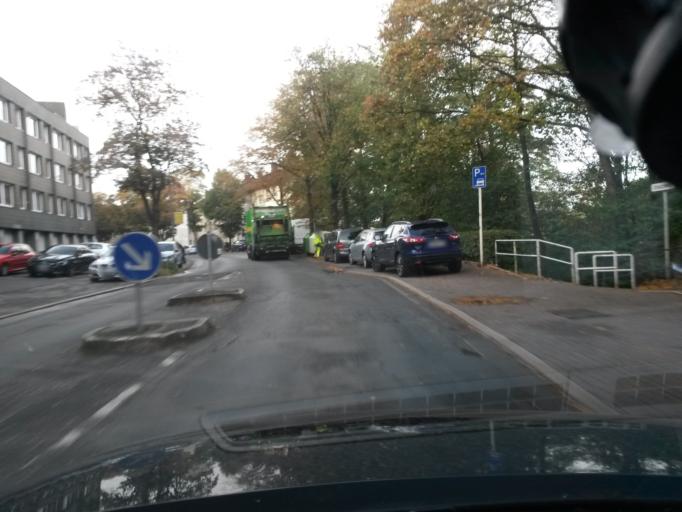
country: DE
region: North Rhine-Westphalia
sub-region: Regierungsbezirk Arnsberg
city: Luedenscheid
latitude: 51.2257
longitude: 7.6416
